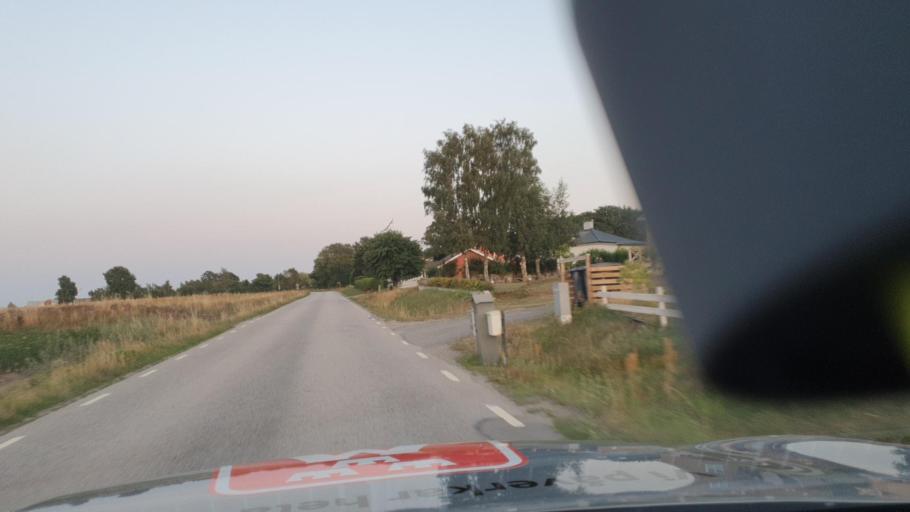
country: SE
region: Blekinge
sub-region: Solvesborgs Kommun
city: Soelvesborg
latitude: 56.0423
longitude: 14.6241
